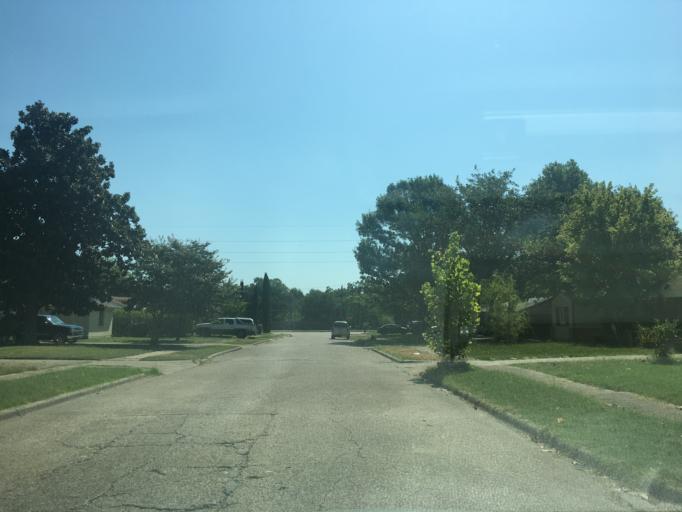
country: US
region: Texas
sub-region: Dallas County
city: Garland
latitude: 32.8550
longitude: -96.6670
